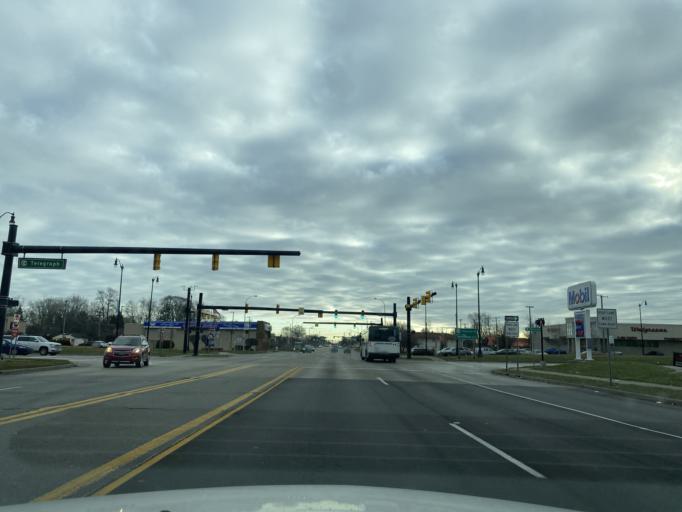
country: US
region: Michigan
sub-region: Wayne County
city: Taylor
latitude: 42.1975
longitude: -83.2687
